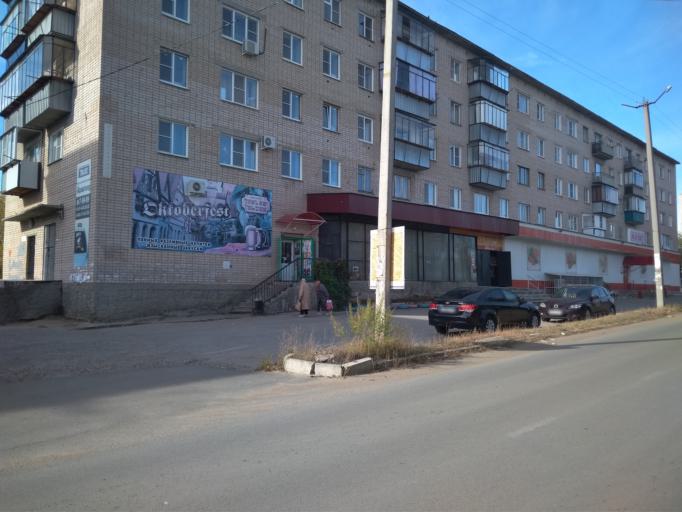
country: RU
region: Chelyabinsk
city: Troitsk
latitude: 54.0507
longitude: 61.6405
